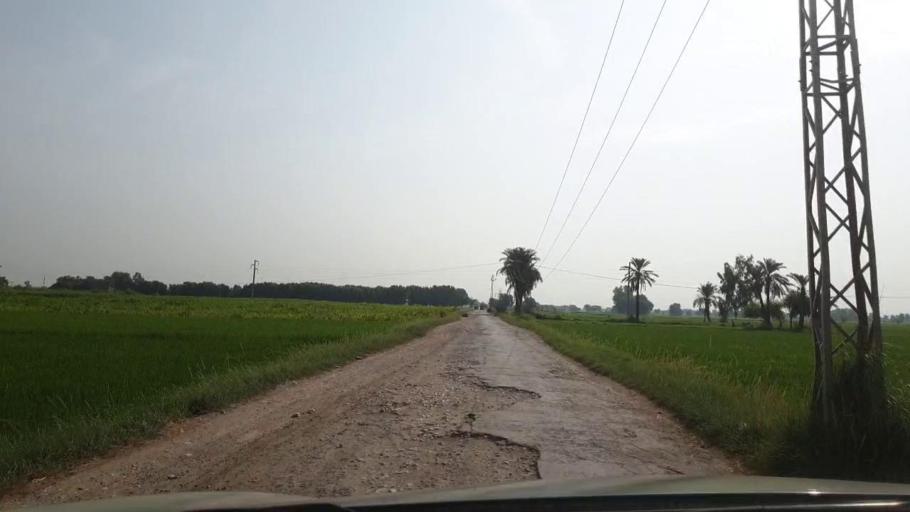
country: PK
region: Sindh
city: Larkana
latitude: 27.4493
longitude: 68.1873
